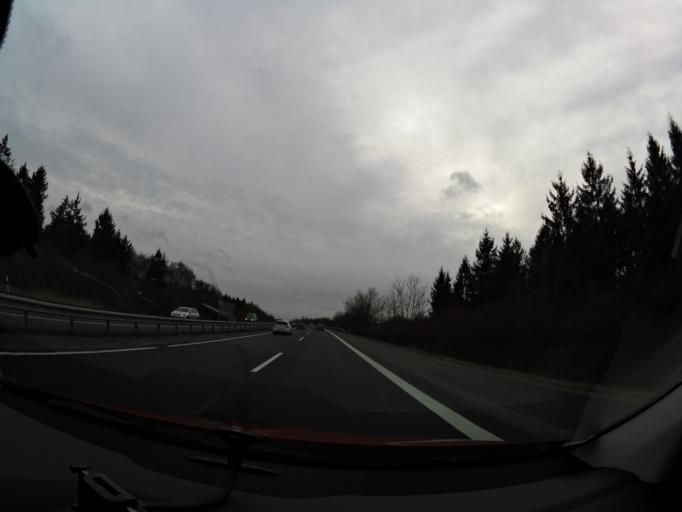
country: DE
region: Lower Saxony
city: Cramme
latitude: 52.1279
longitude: 10.4872
